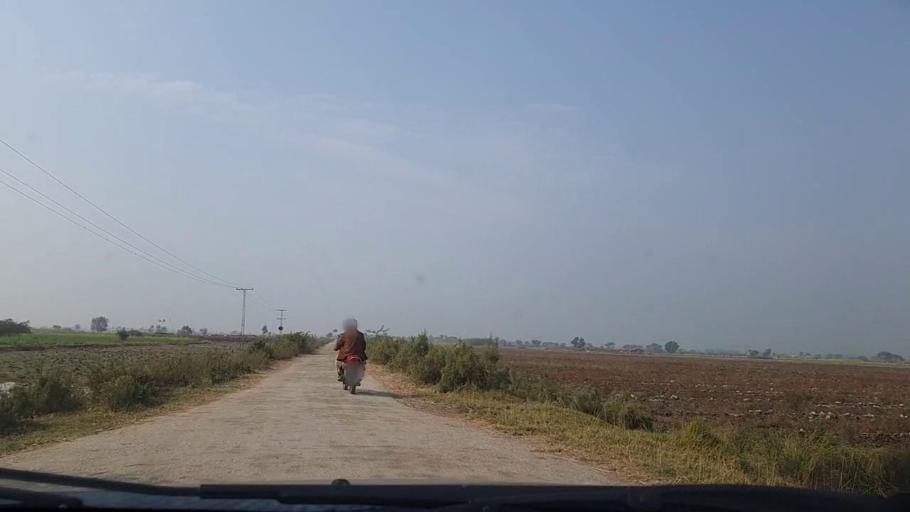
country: PK
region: Sindh
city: Sanghar
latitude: 26.0752
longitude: 68.9583
